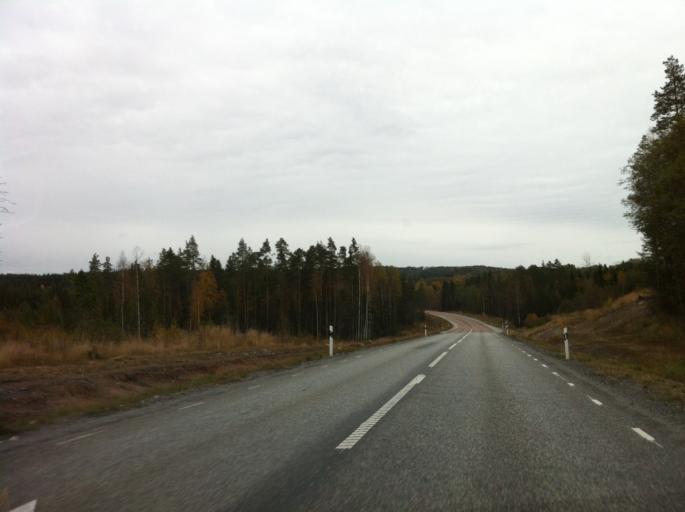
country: SE
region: OErebro
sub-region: Ljusnarsbergs Kommun
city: Kopparberg
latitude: 59.9810
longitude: 15.0205
